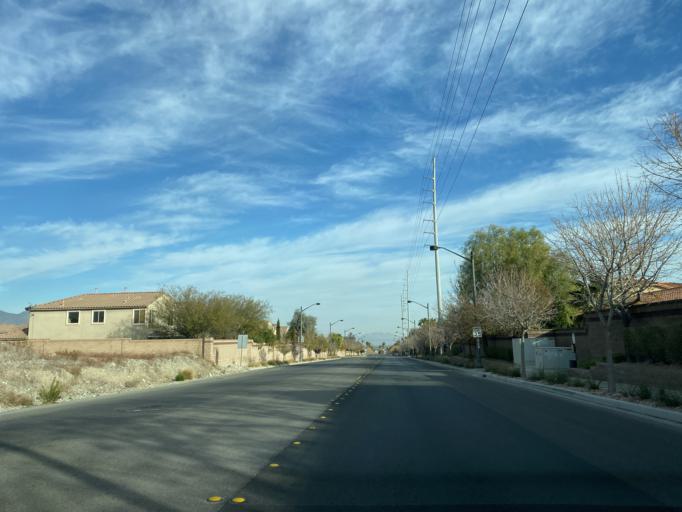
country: US
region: Nevada
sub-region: Clark County
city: Summerlin South
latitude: 36.2992
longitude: -115.3008
